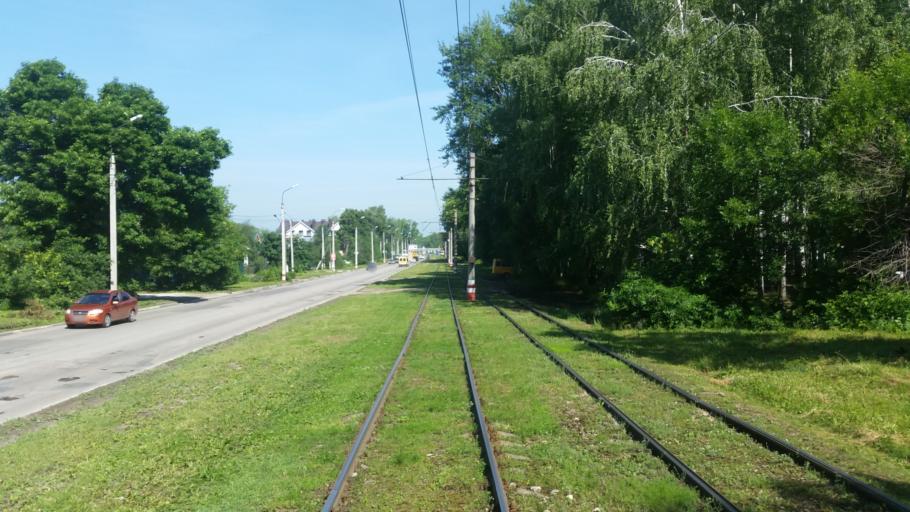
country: RU
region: Ulyanovsk
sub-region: Ulyanovskiy Rayon
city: Ulyanovsk
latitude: 54.3537
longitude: 48.3791
